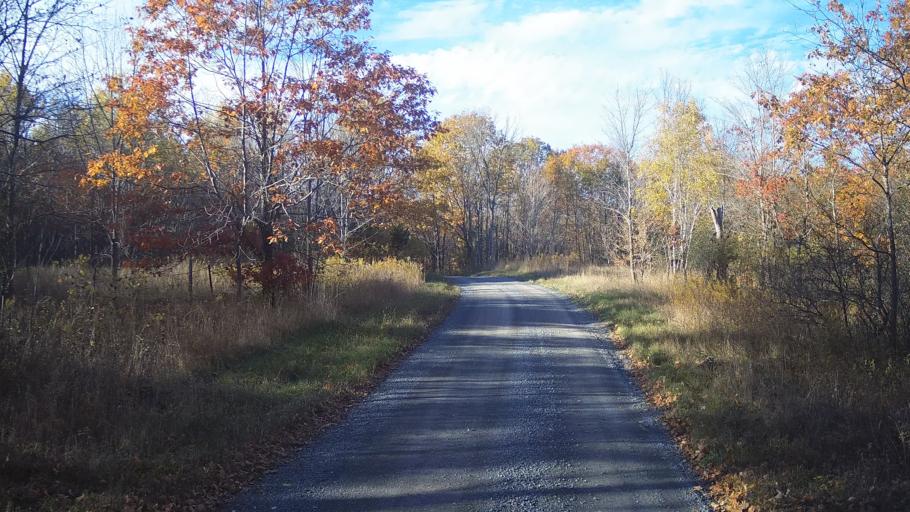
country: CA
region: Ontario
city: Perth
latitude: 44.7257
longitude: -76.4398
